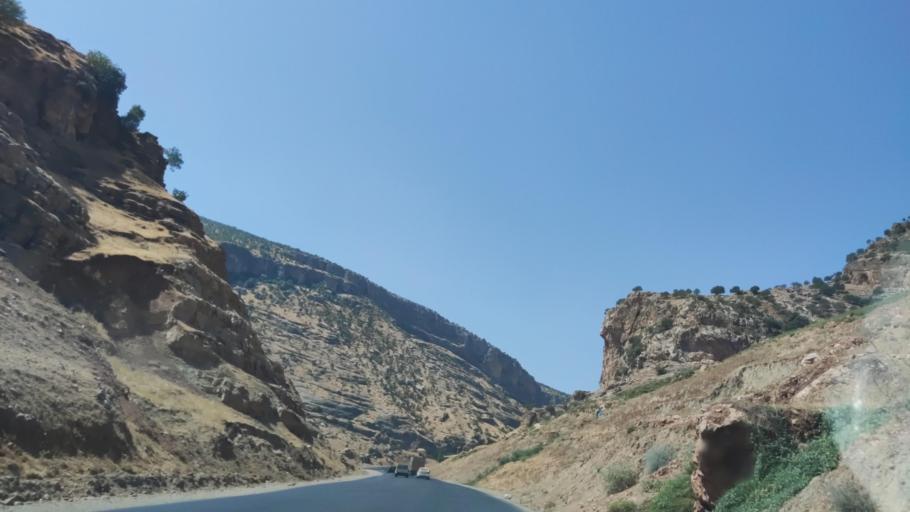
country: IQ
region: Arbil
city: Ruwandiz
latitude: 36.6327
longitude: 44.4447
